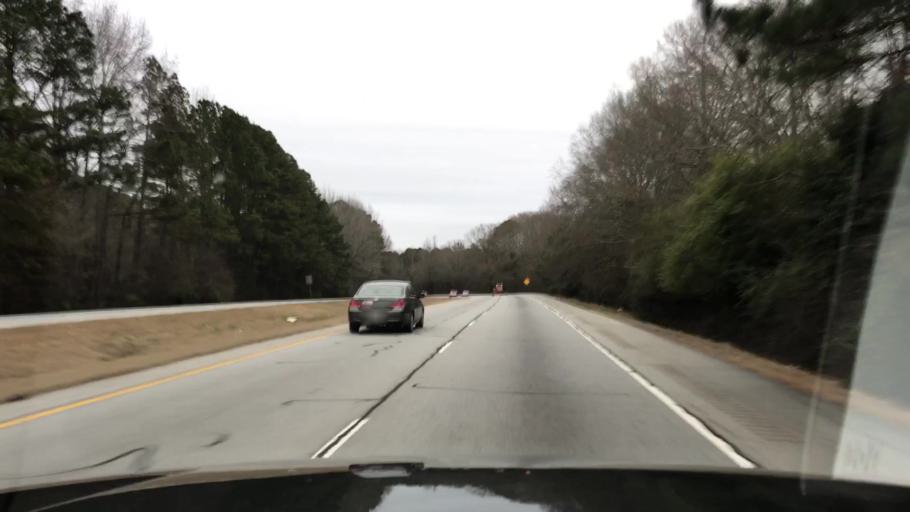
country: US
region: Georgia
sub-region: Walton County
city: Monroe
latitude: 33.8044
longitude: -83.7011
